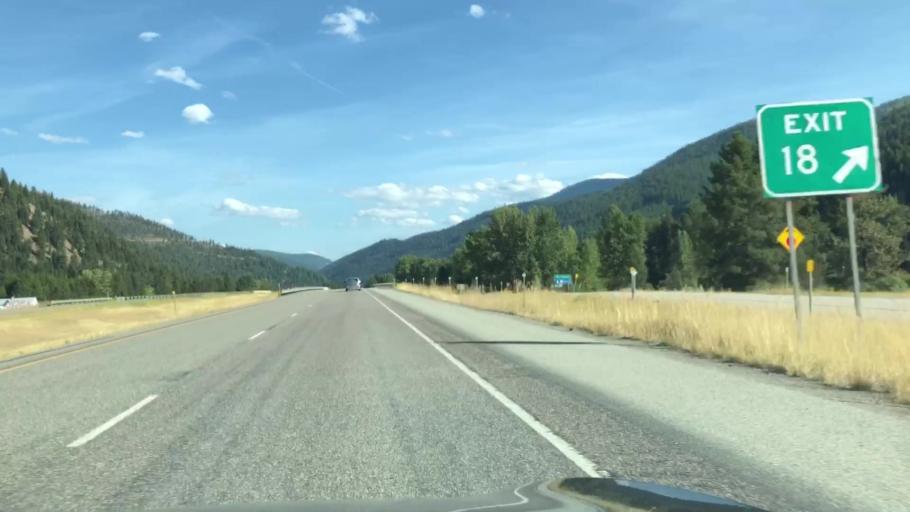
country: US
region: Montana
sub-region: Sanders County
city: Thompson Falls
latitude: 47.3765
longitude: -115.3542
